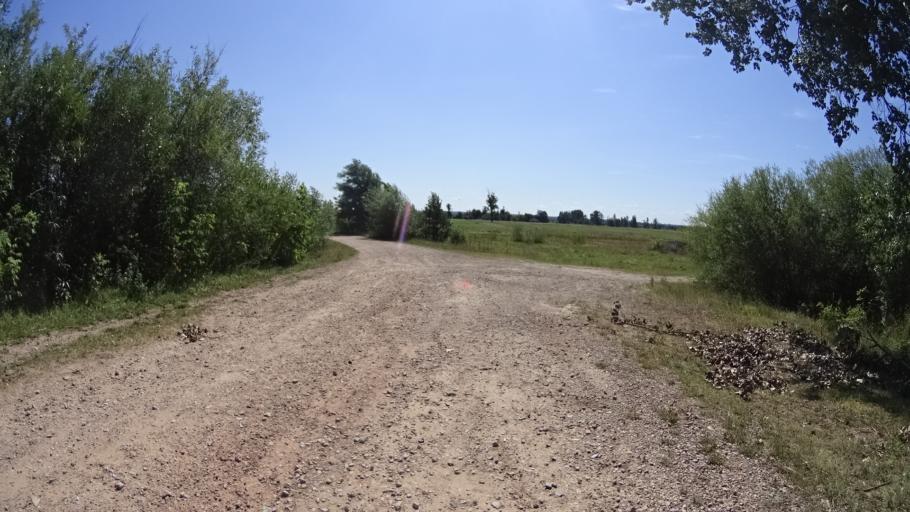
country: PL
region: Masovian Voivodeship
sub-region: Powiat bialobrzeski
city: Bialobrzegi
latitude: 51.6647
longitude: 20.8884
